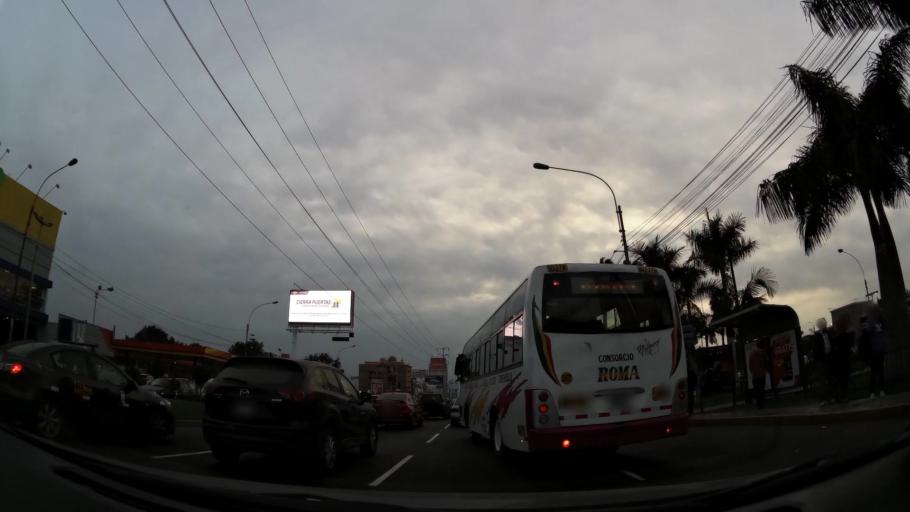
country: PE
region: Callao
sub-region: Callao
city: Callao
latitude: -12.0779
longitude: -77.0838
